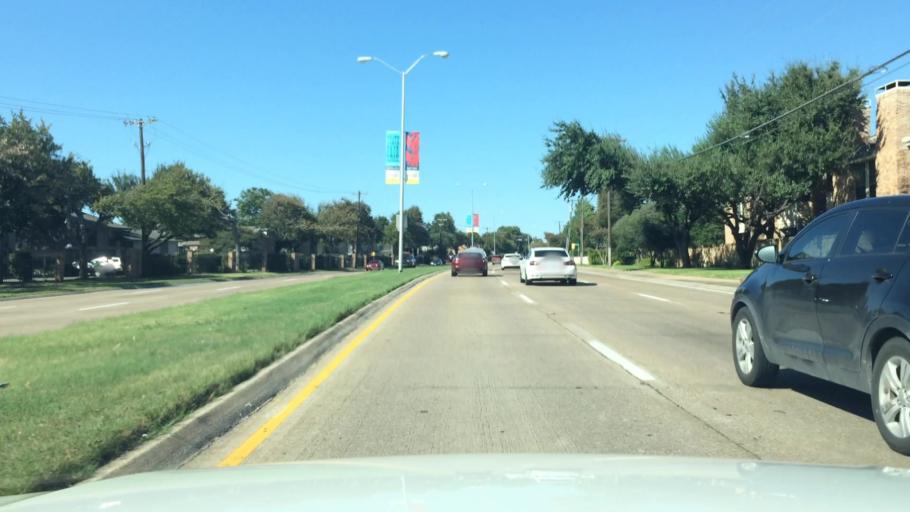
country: US
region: Texas
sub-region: Dallas County
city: Addison
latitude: 32.9552
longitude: -96.8044
